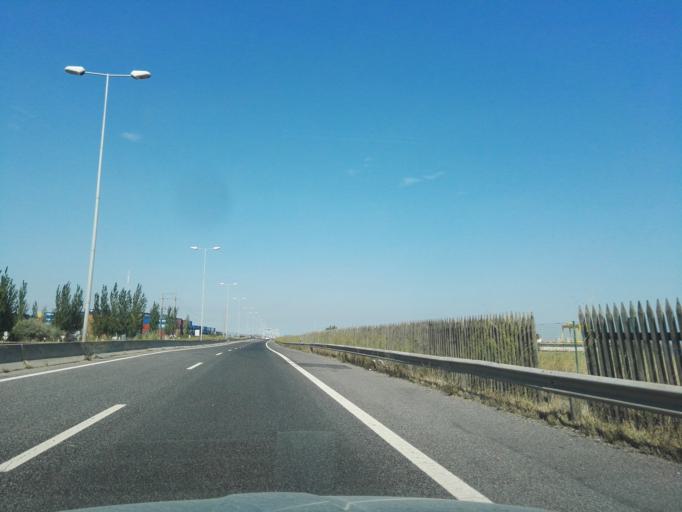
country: PT
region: Lisbon
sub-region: Loures
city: Sao Joao da Talha
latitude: 38.8266
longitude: -9.0822
